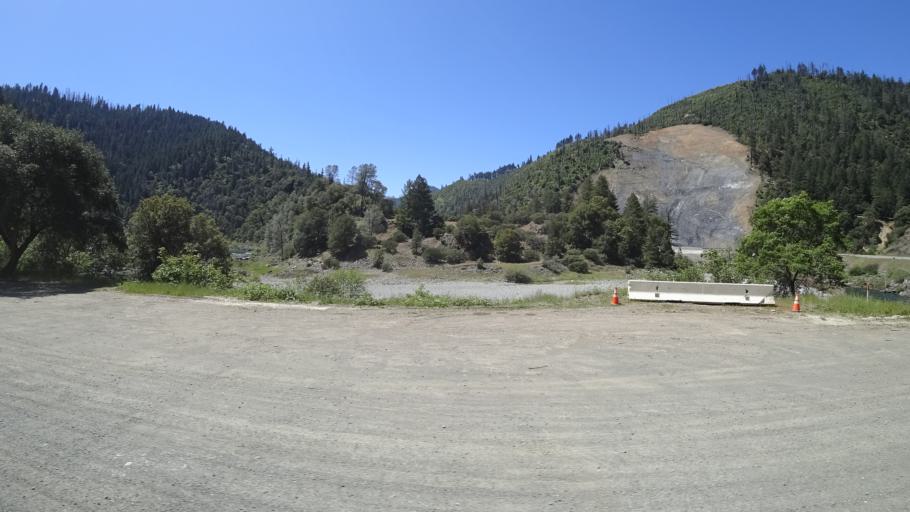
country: US
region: California
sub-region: Trinity County
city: Hayfork
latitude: 40.7780
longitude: -123.3071
